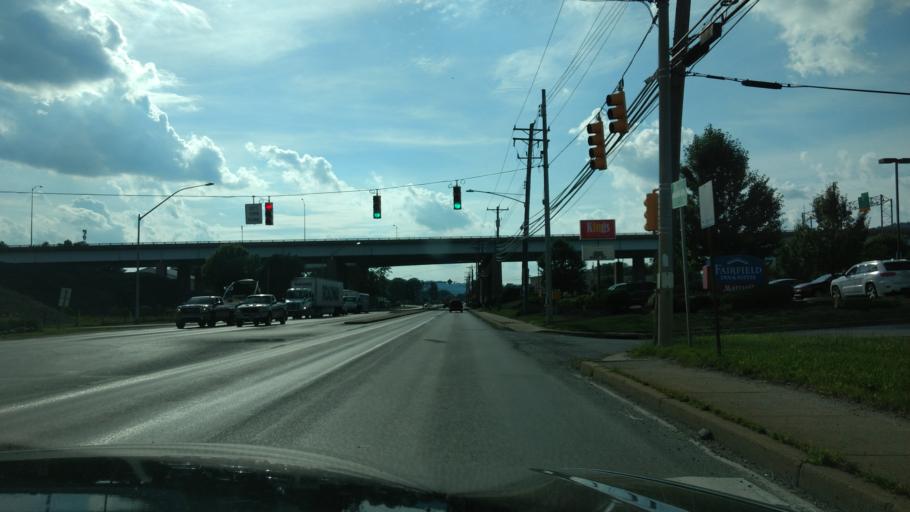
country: US
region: Pennsylvania
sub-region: Allegheny County
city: Coraopolis
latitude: 40.5125
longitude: -80.1329
